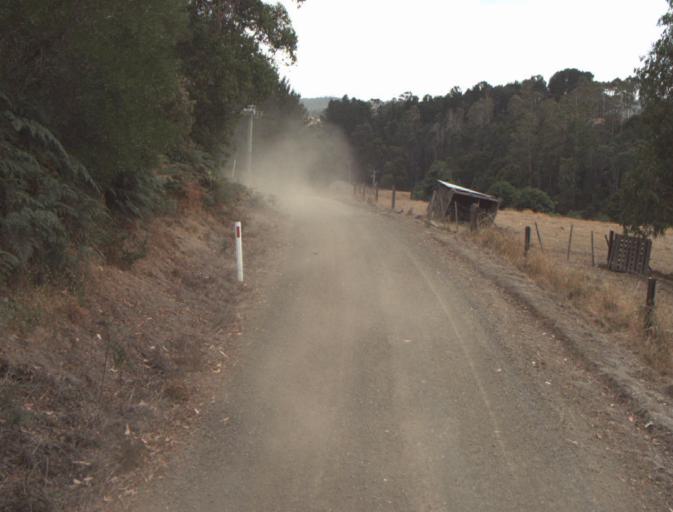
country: AU
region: Tasmania
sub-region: Launceston
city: Mayfield
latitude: -41.1625
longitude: 147.2115
